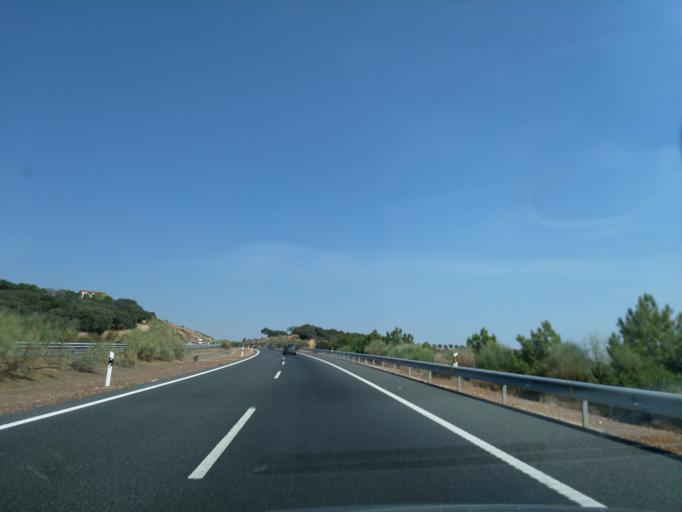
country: ES
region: Extremadura
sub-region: Provincia de Badajoz
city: Aljucen
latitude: 39.0672
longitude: -6.3141
